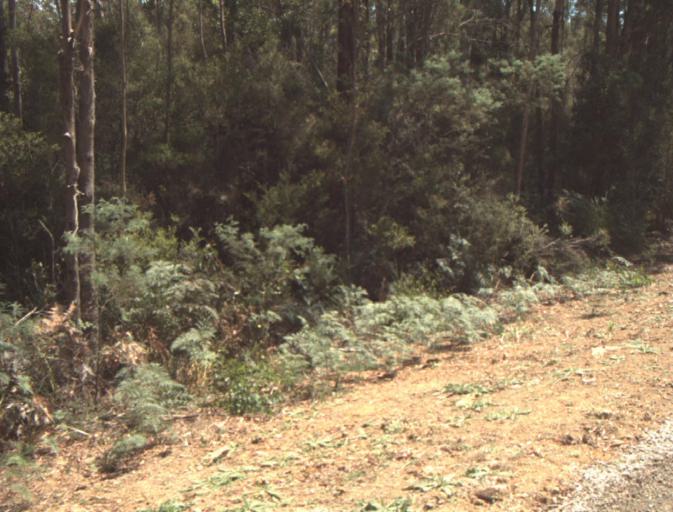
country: AU
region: Tasmania
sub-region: Launceston
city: Mayfield
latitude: -41.2791
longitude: 147.1173
